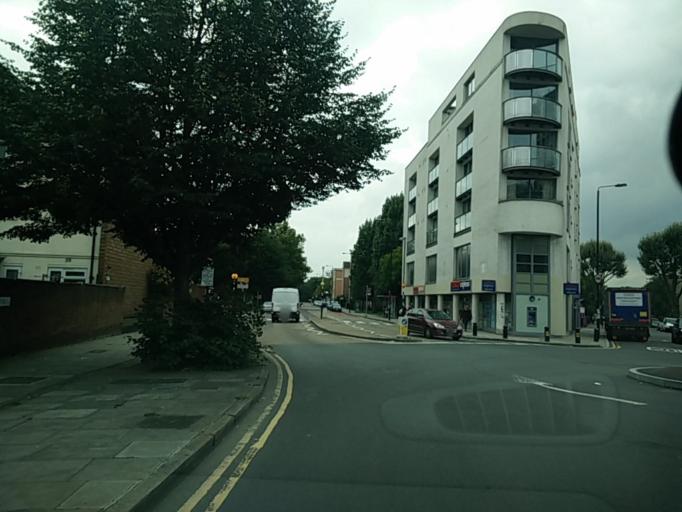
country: GB
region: England
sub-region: Greater London
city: Poplar
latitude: 51.4998
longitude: -0.0093
